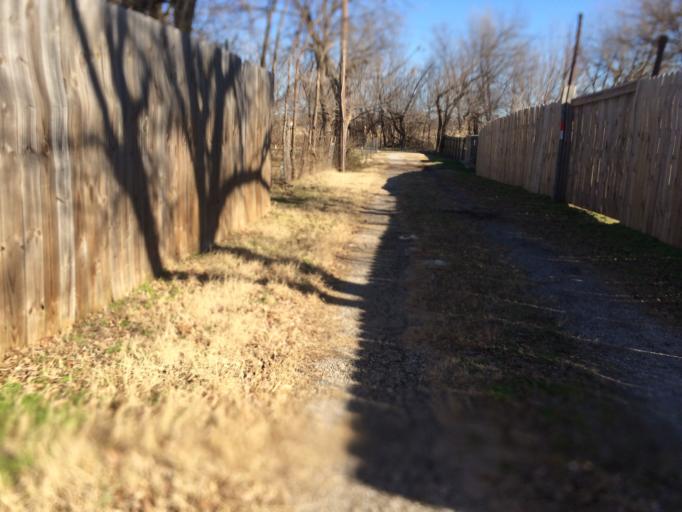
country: US
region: Oklahoma
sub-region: Cleveland County
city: Norman
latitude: 35.2215
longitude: -97.4298
